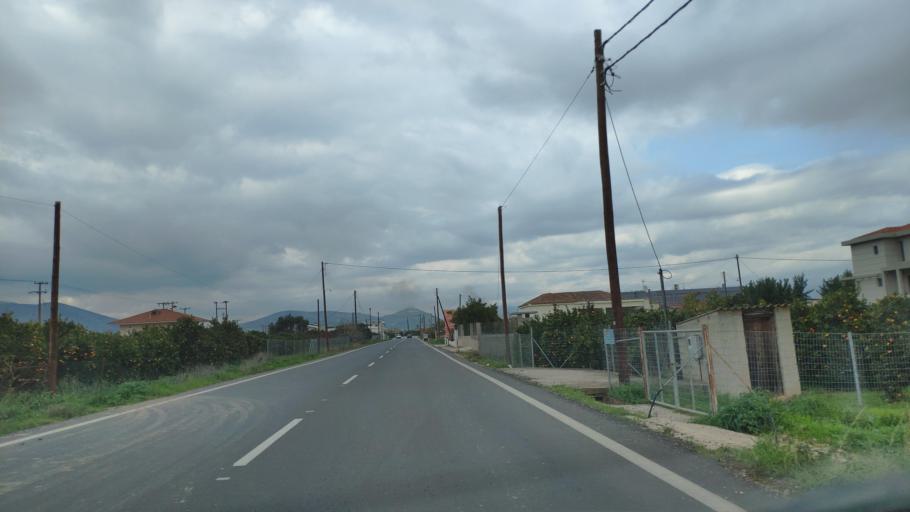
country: GR
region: Peloponnese
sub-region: Nomos Argolidos
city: Nea Kios
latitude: 37.5748
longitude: 22.7084
